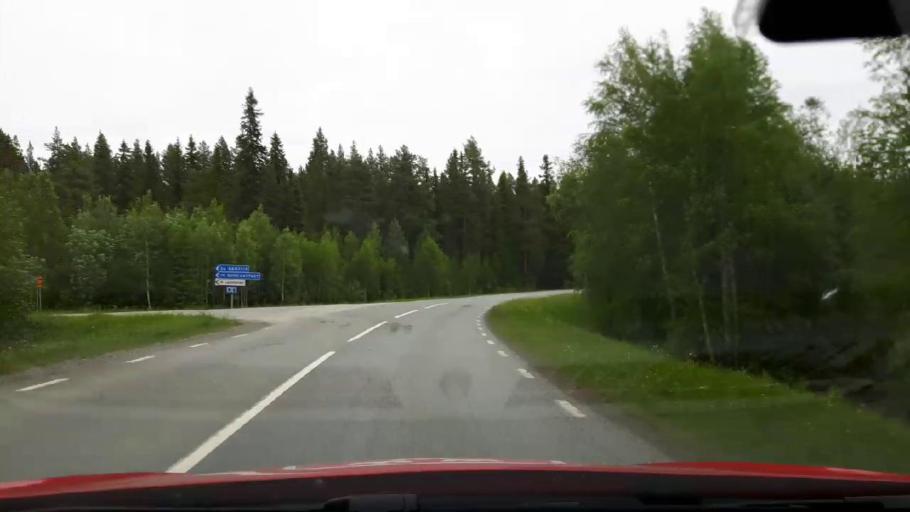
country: SE
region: Jaemtland
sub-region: Stroemsunds Kommun
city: Stroemsund
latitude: 63.3913
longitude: 15.6733
